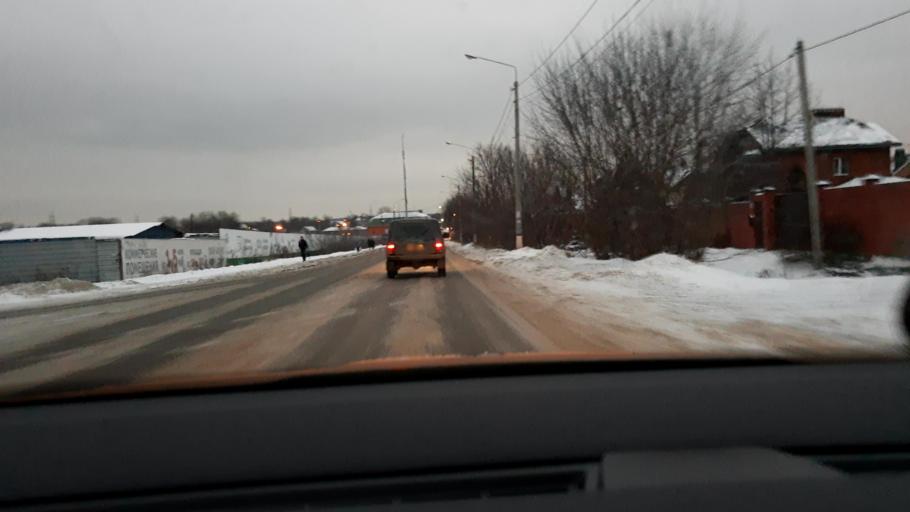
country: RU
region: Moskovskaya
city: Tomilino
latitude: 55.6410
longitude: 37.9435
